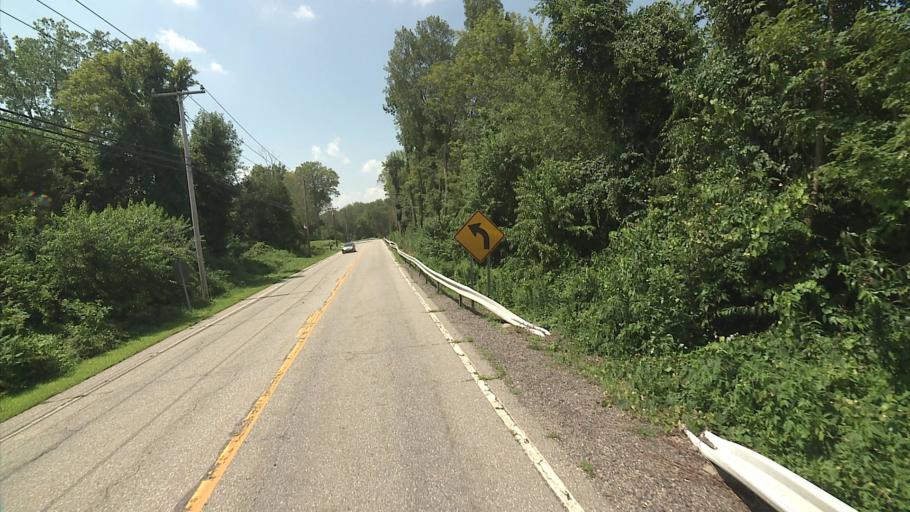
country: US
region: Connecticut
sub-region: New London County
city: Preston City
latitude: 41.5320
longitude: -72.0001
